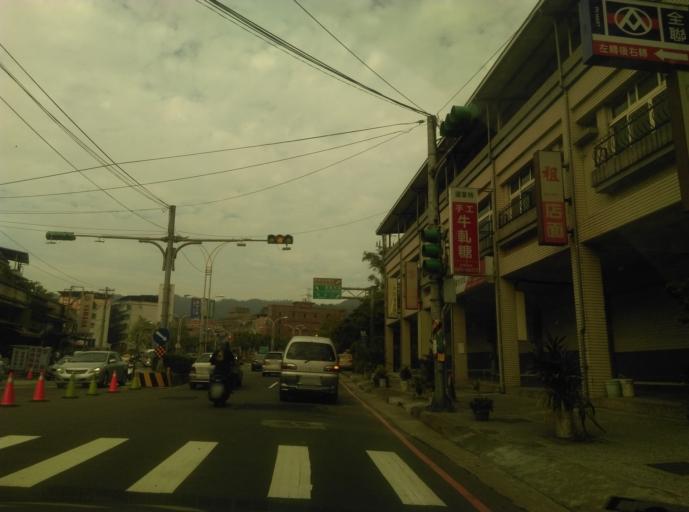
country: TW
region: Taiwan
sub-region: Keelung
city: Keelung
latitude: 25.1547
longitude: 121.6968
